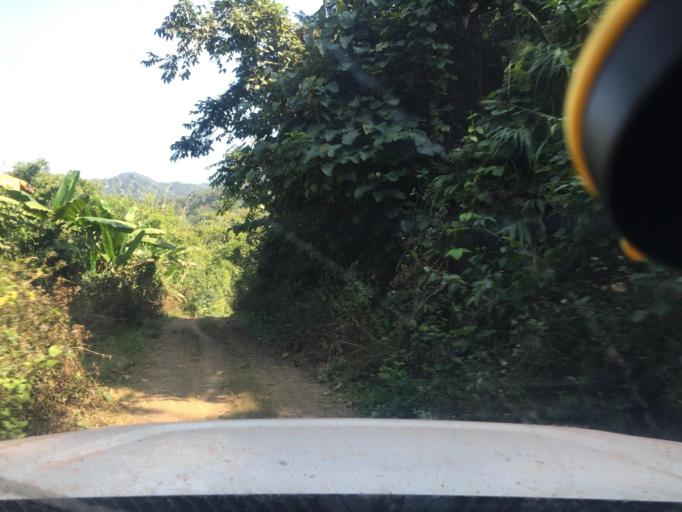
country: LA
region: Phongsali
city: Phongsali
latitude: 21.6845
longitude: 102.4080
